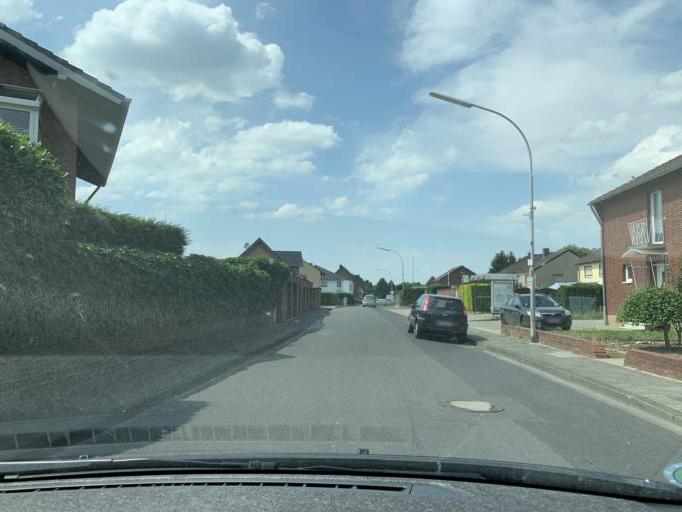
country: DE
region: North Rhine-Westphalia
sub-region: Regierungsbezirk Dusseldorf
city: Grevenbroich
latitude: 51.0434
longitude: 6.5815
